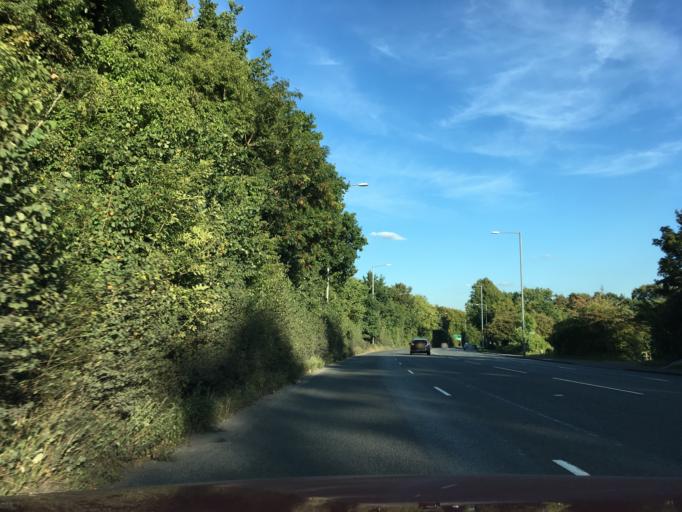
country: GB
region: England
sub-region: North Somerset
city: Easton-in-Gordano
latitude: 51.4883
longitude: -2.6597
